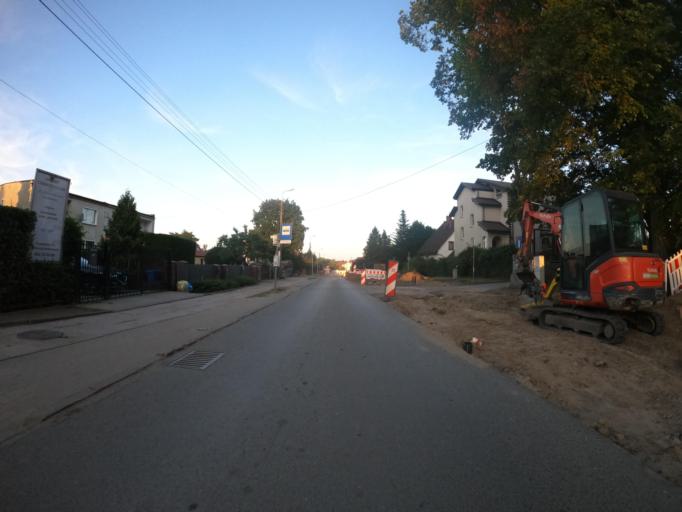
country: PL
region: West Pomeranian Voivodeship
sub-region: Powiat policki
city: Przeclaw
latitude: 53.4557
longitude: 14.4682
